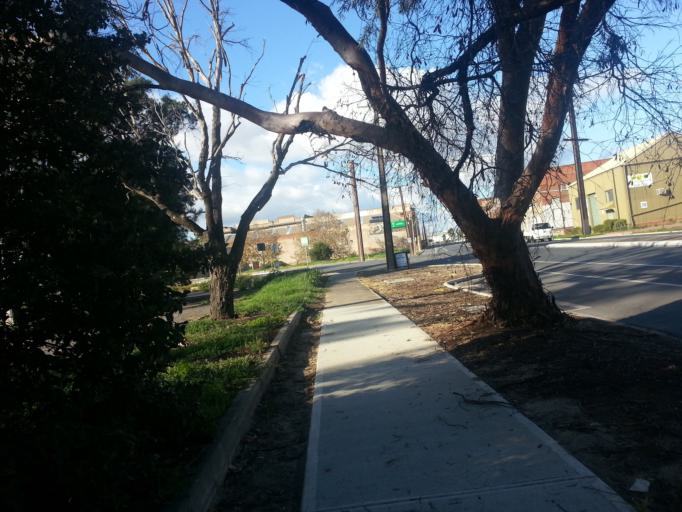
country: AU
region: South Australia
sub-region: Port Adelaide Enfield
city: Birkenhead
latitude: -34.8434
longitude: 138.5098
